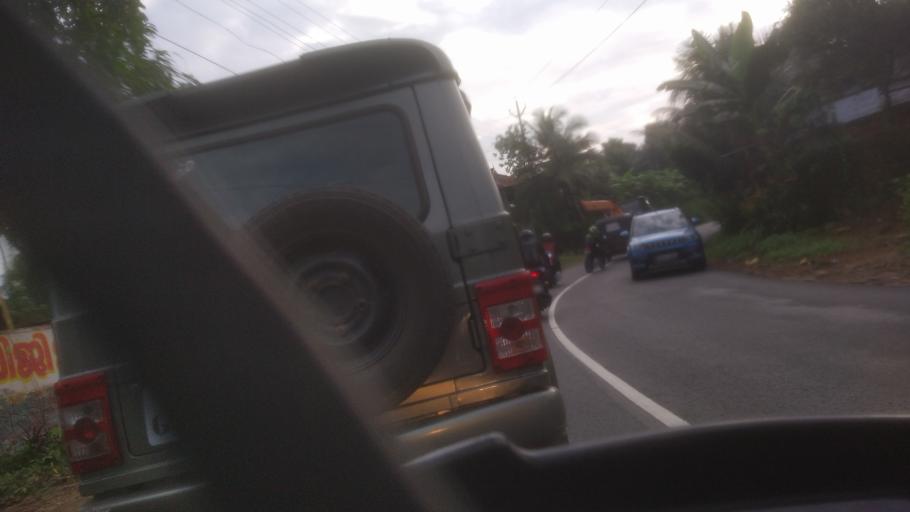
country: IN
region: Kerala
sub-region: Ernakulam
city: Kotamangalam
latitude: 10.0599
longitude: 76.6414
